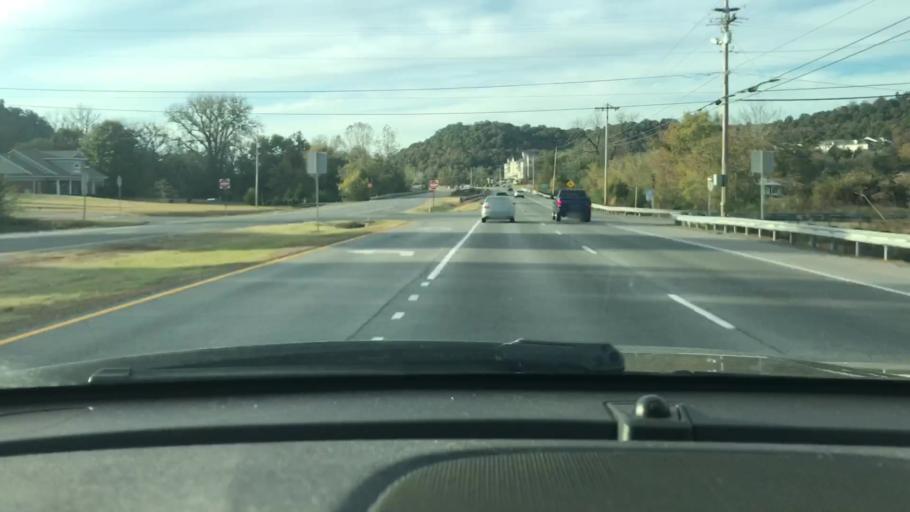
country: US
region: Tennessee
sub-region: Cheatham County
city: Ashland City
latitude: 36.2399
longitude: -87.0224
